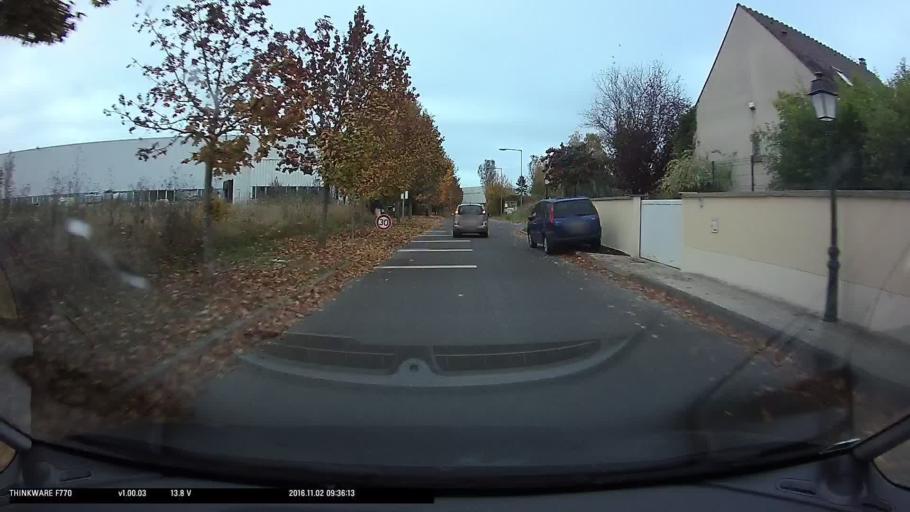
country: FR
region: Ile-de-France
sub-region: Departement du Val-d'Oise
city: Vaureal
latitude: 49.0566
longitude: 2.0234
